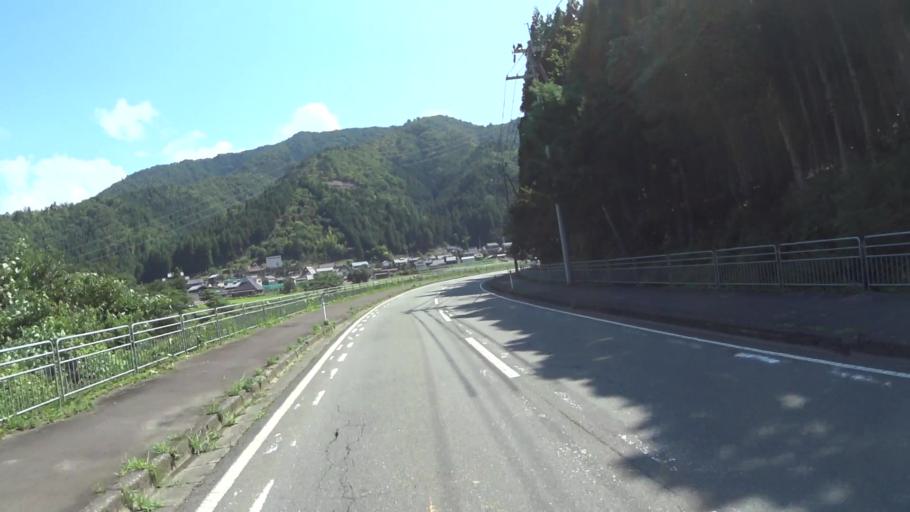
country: JP
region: Fukui
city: Obama
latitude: 35.4040
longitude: 135.6881
